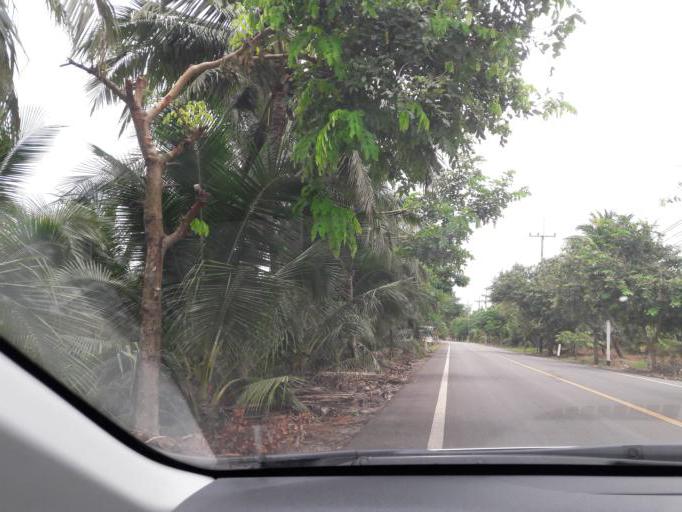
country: TH
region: Samut Sakhon
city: Ban Phaeo
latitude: 13.6075
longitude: 100.0223
